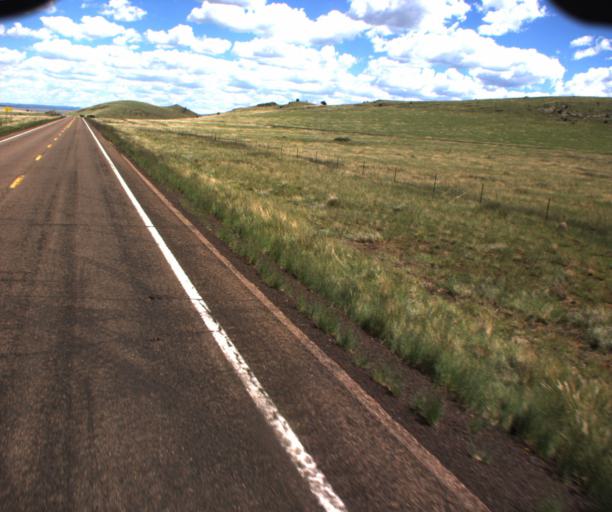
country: US
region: Arizona
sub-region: Apache County
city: Springerville
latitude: 34.2127
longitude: -109.4400
